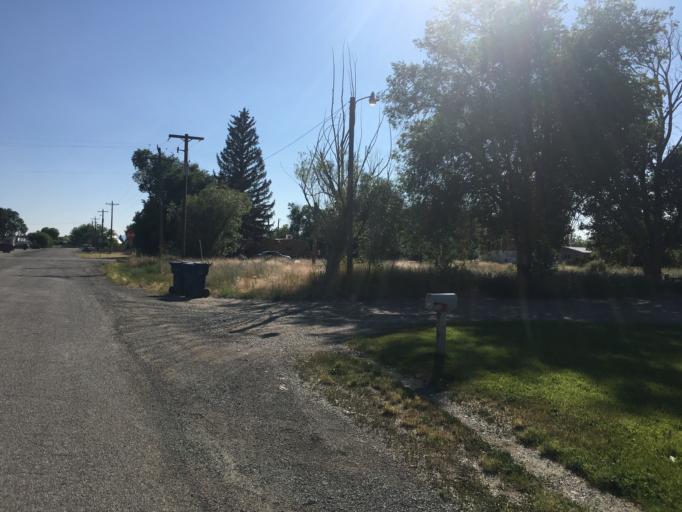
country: US
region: Idaho
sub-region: Butte County
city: Arco
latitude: 43.6328
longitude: -113.2968
